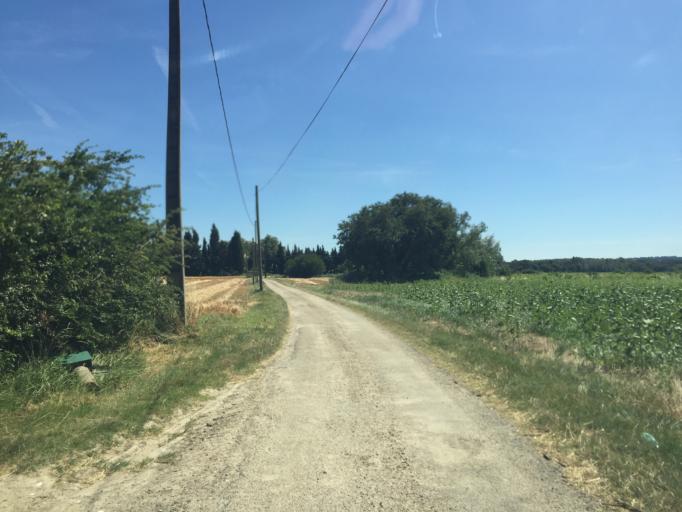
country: FR
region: Provence-Alpes-Cote d'Azur
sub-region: Departement du Vaucluse
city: Courthezon
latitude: 44.0803
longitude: 4.9018
